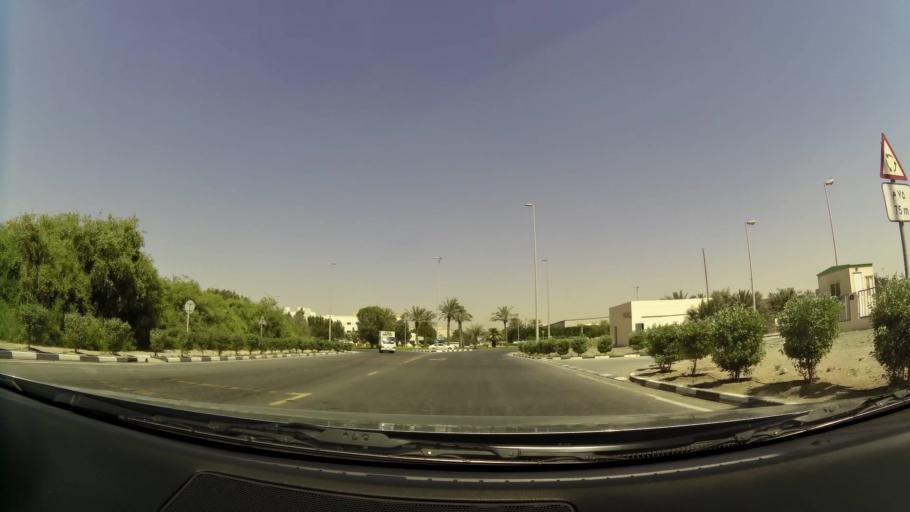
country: AE
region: Dubai
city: Dubai
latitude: 24.9733
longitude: 55.1626
